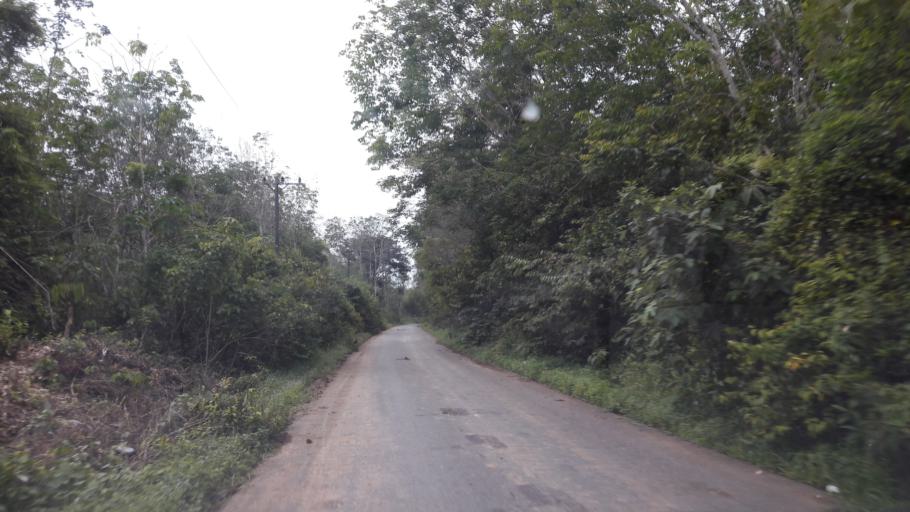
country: ID
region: South Sumatra
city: Gunungmenang
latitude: -3.1192
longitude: 104.1177
